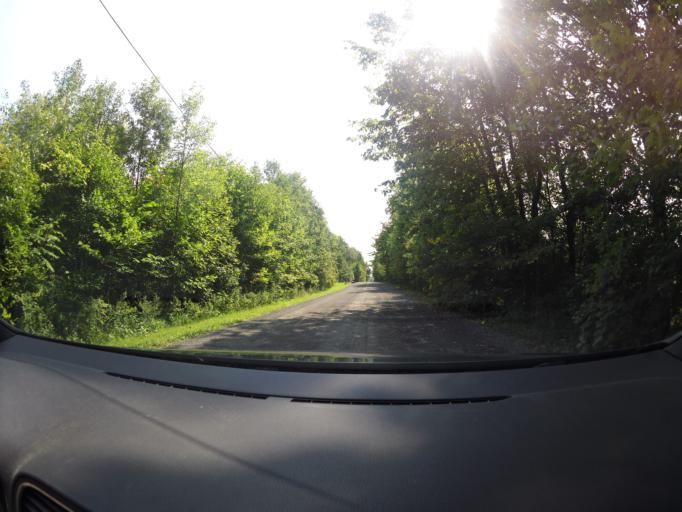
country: CA
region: Ontario
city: Arnprior
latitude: 45.4692
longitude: -76.1800
